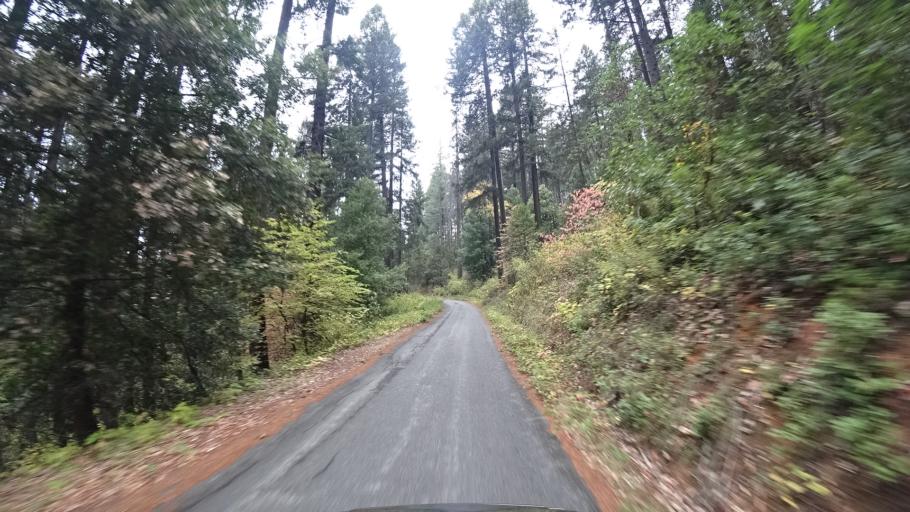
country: US
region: California
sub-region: Siskiyou County
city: Happy Camp
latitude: 41.8040
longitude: -123.3396
